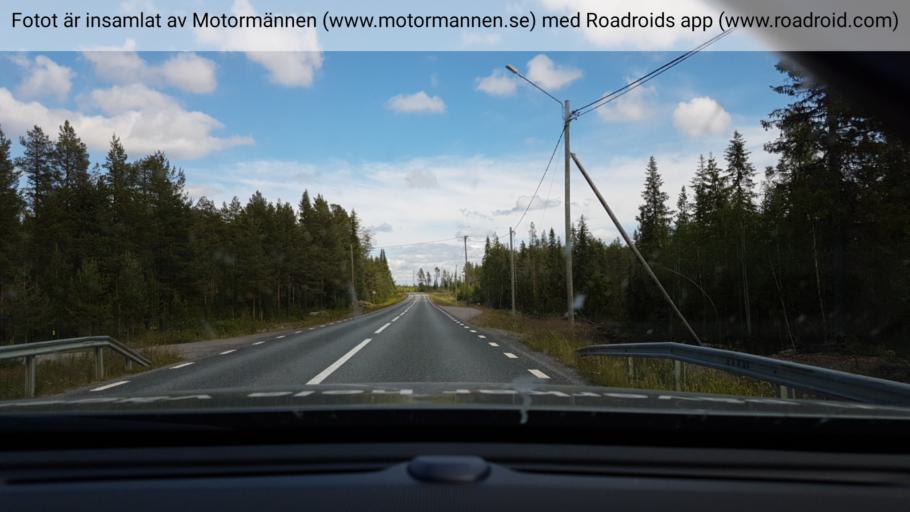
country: SE
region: Vaesterbotten
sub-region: Sorsele Kommun
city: Sorsele
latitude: 65.5566
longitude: 17.8610
